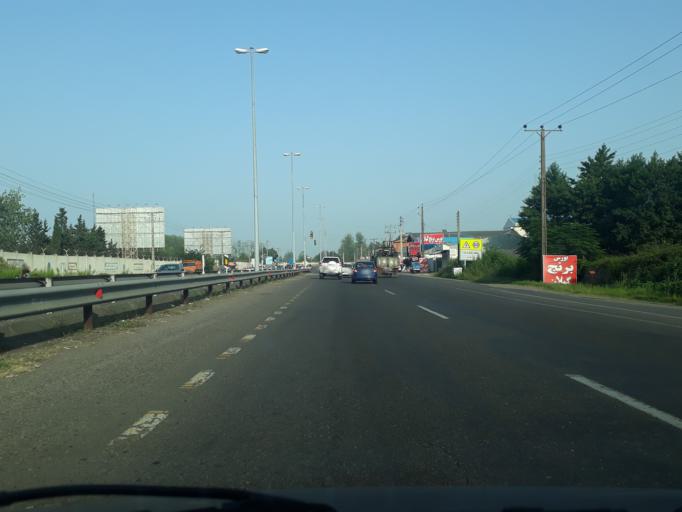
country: IR
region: Gilan
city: Bandar-e Anzali
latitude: 37.4577
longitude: 49.6081
